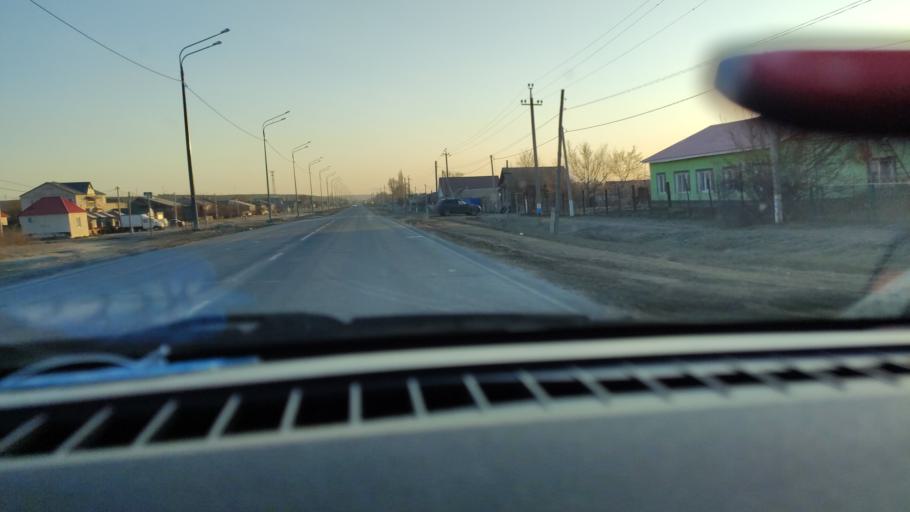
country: RU
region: Saratov
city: Sinodskoye
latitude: 51.9904
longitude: 46.6680
